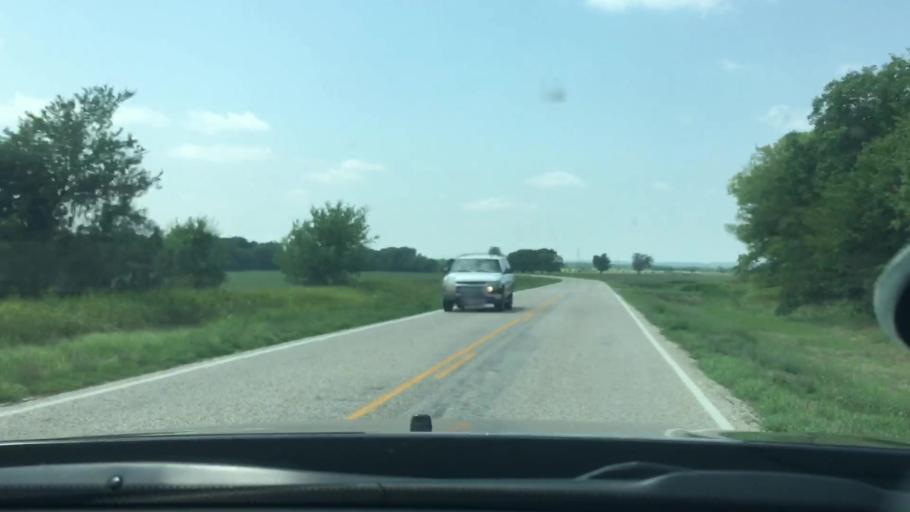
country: US
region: Oklahoma
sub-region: Johnston County
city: Tishomingo
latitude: 34.3746
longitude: -96.4636
